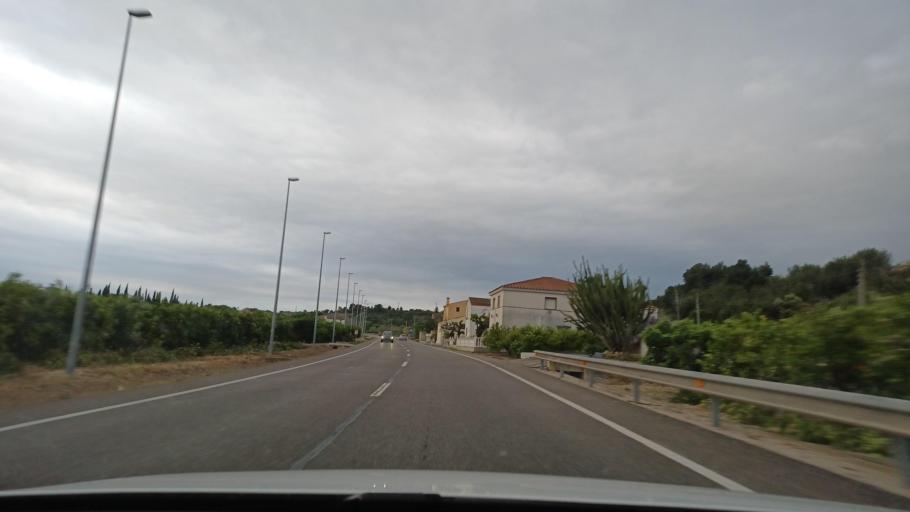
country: ES
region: Catalonia
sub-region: Provincia de Tarragona
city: Tortosa
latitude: 40.7811
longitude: 0.5042
